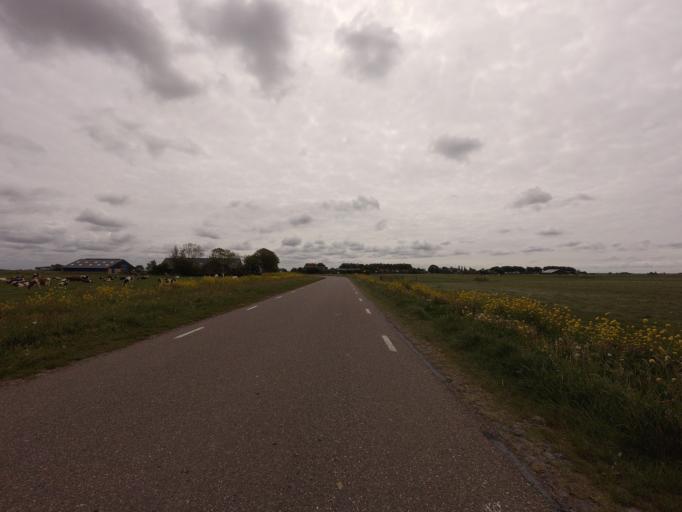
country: NL
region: Friesland
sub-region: Sudwest Fryslan
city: Workum
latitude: 52.9557
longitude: 5.4965
